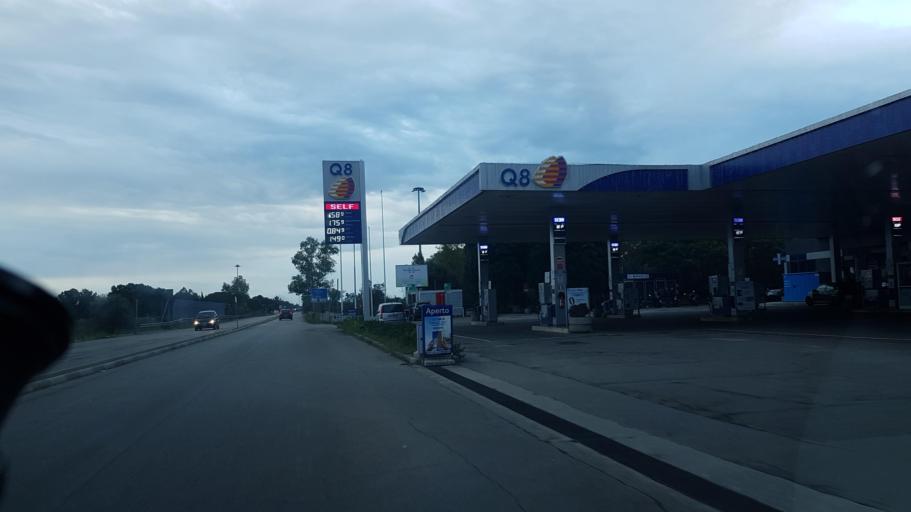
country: IT
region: Apulia
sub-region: Provincia di Lecce
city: Merine
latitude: 40.3446
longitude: 18.2022
